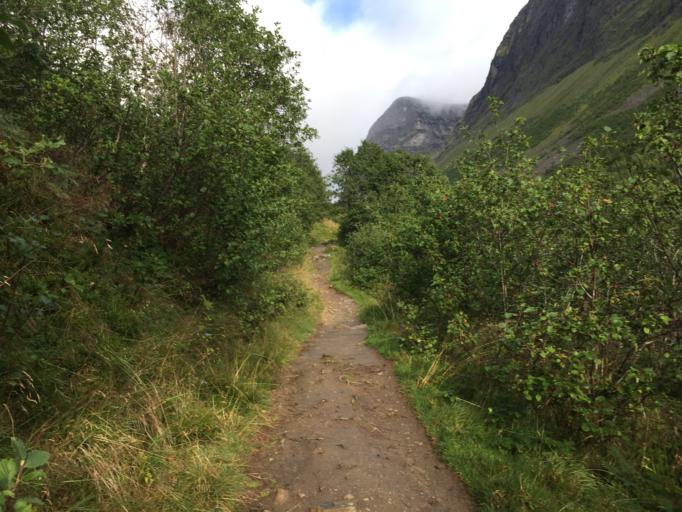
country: NO
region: More og Romsdal
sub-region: Norddal
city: Valldal
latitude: 62.1055
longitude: 7.2300
